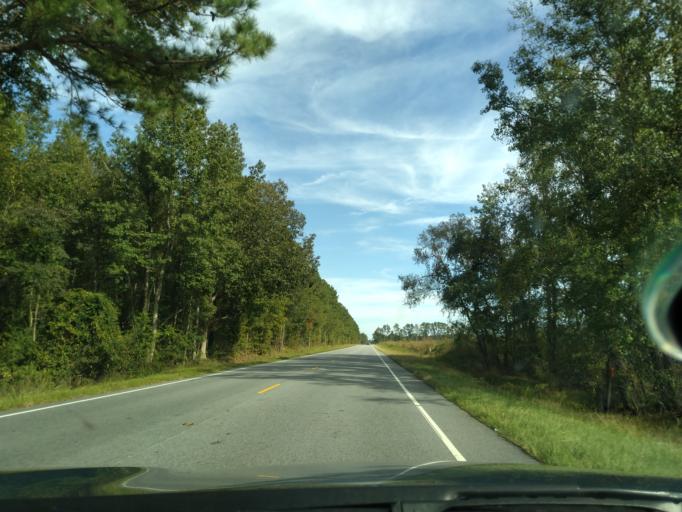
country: US
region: North Carolina
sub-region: Beaufort County
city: River Road
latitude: 35.5244
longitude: -76.8567
